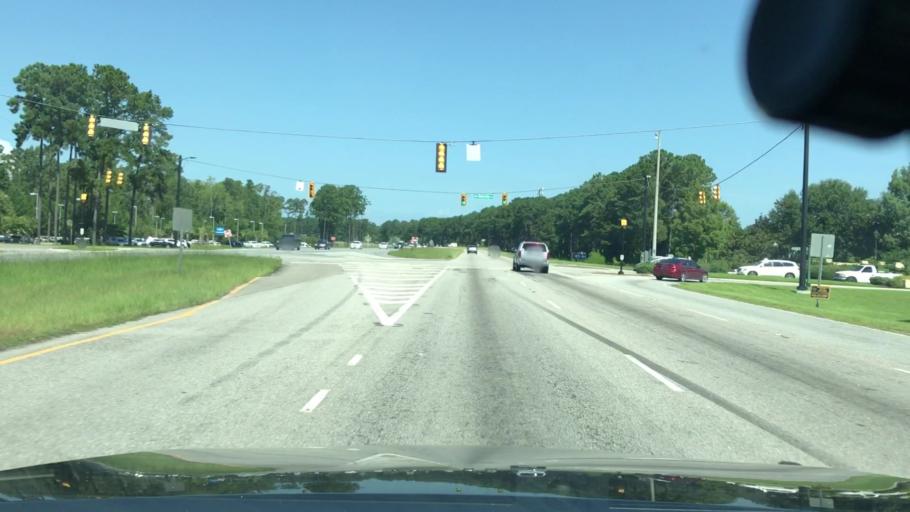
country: US
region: South Carolina
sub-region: Jasper County
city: Hardeeville
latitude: 32.3076
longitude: -80.9757
